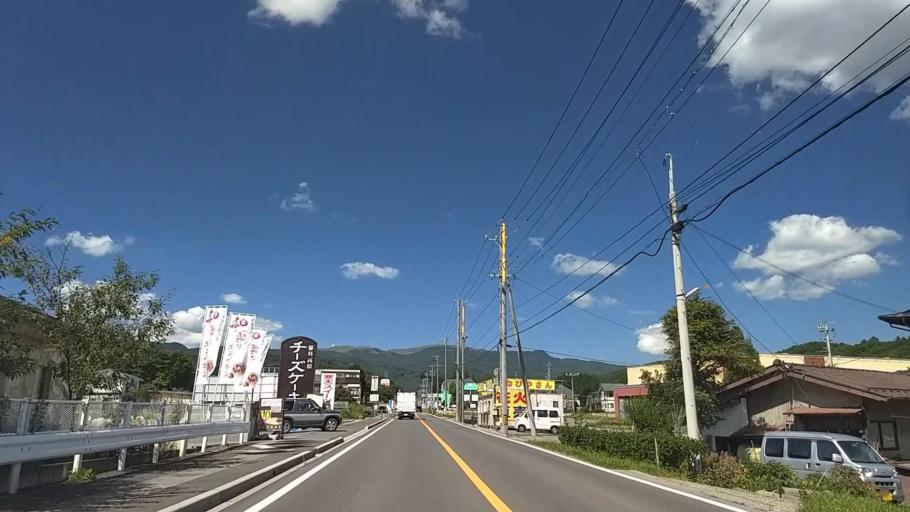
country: JP
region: Nagano
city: Chino
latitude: 36.0092
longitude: 138.1751
